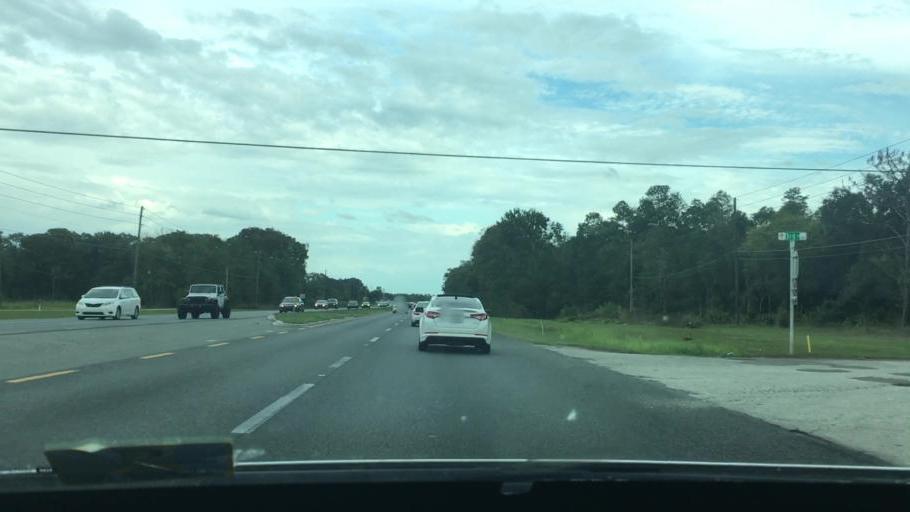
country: US
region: Florida
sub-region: Orange County
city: Bithlo
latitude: 28.5552
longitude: -81.1120
